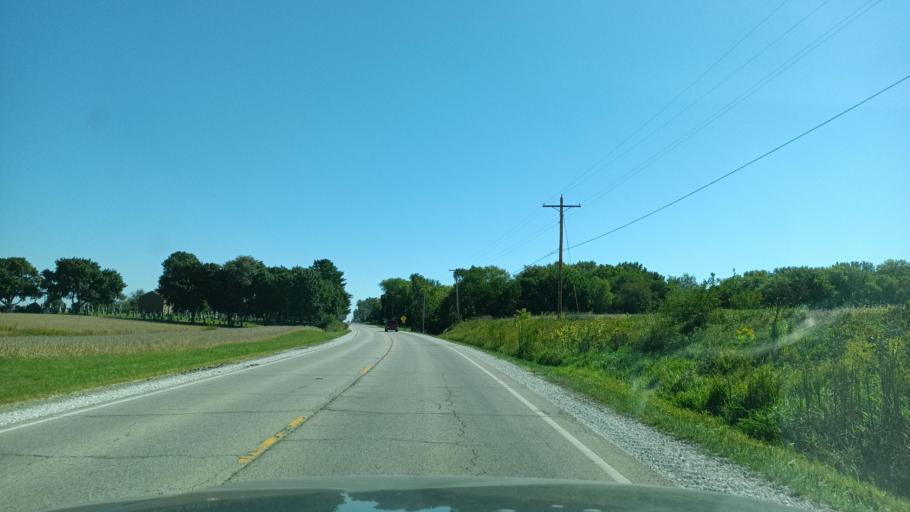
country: US
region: Illinois
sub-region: Peoria County
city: Hanna City
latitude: 40.7900
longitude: -89.7592
